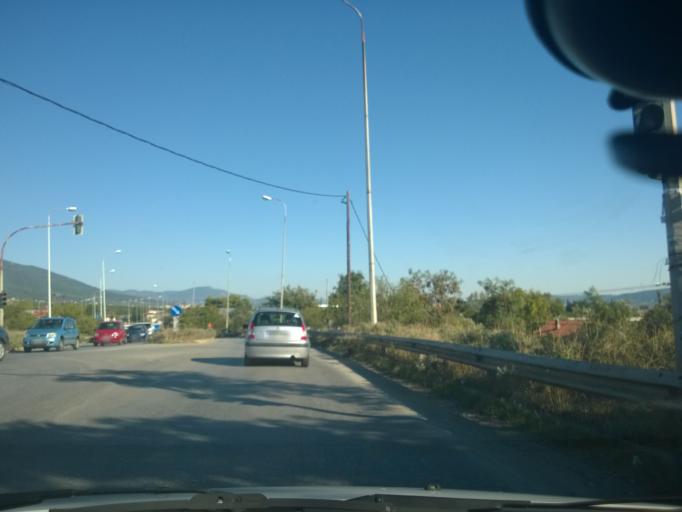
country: GR
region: Central Macedonia
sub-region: Nomos Thessalonikis
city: Thermi
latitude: 40.5390
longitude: 23.0096
